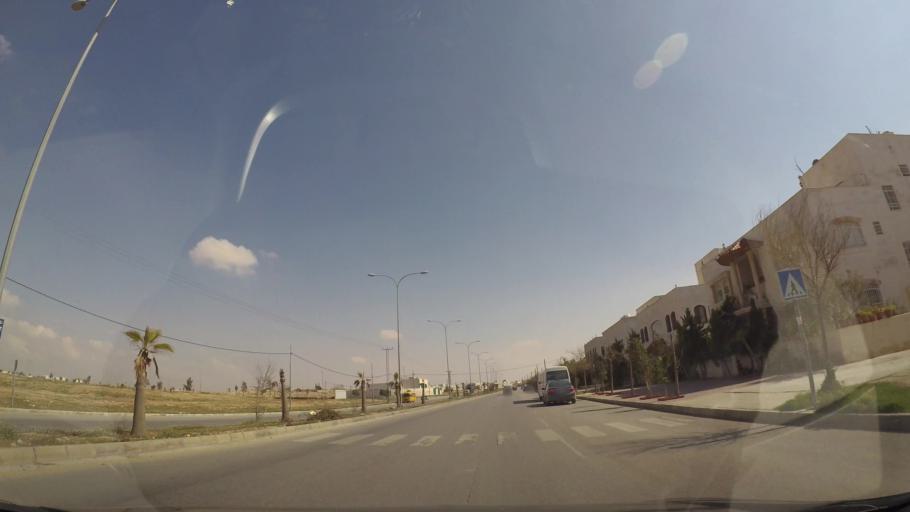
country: JO
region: Zarqa
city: Zarqa
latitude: 32.0657
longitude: 36.1091
